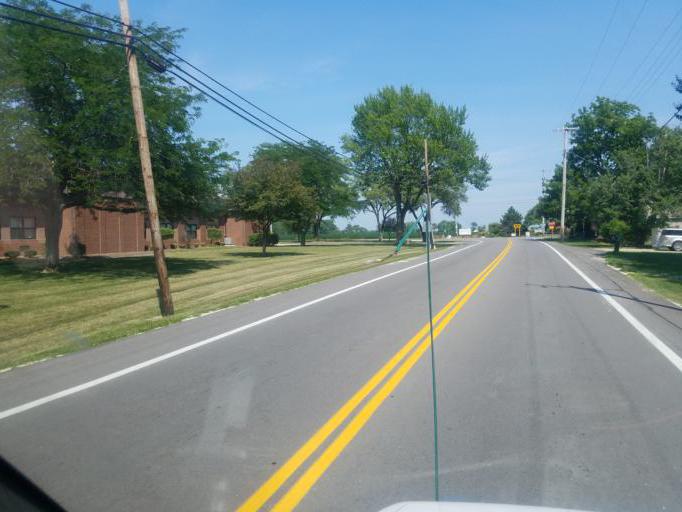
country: US
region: Ohio
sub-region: Mercer County
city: Celina
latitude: 40.4890
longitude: -84.5422
